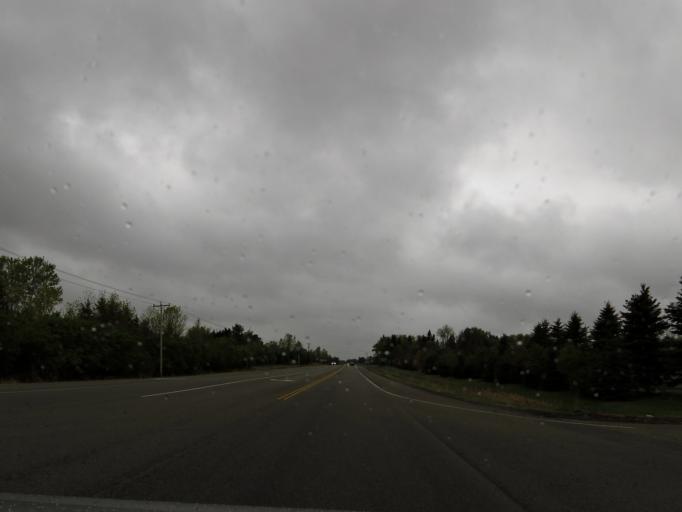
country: US
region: Minnesota
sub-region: Washington County
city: Lake Elmo
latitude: 45.0242
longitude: -92.8573
